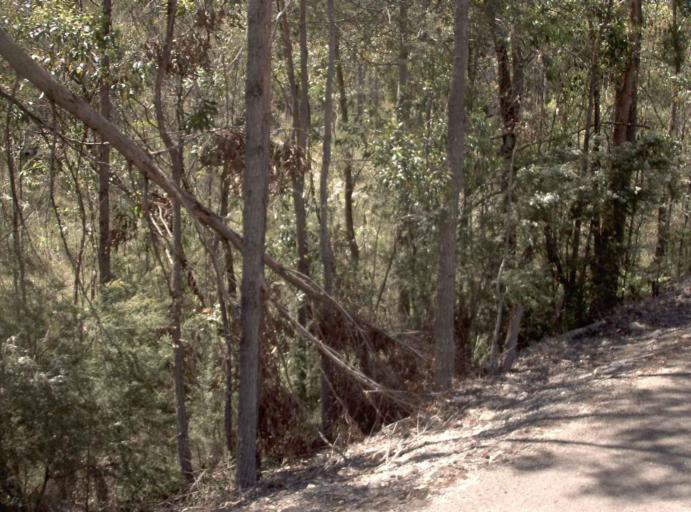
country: AU
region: Victoria
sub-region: East Gippsland
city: Lakes Entrance
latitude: -37.7008
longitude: 148.6068
